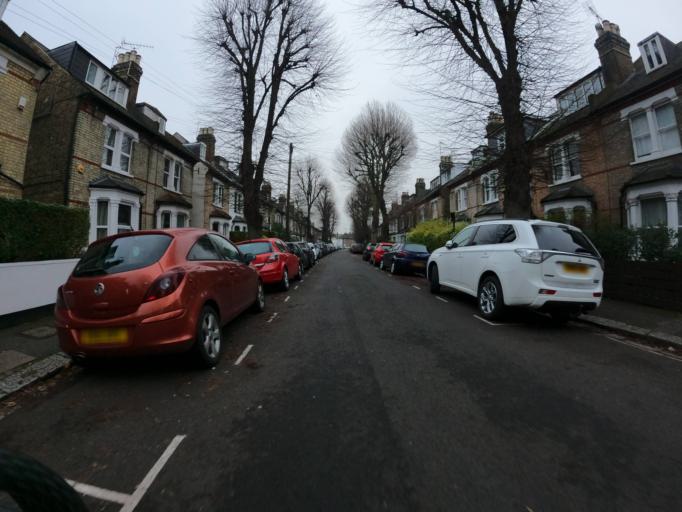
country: GB
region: England
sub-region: Greater London
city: Brentford
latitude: 51.4916
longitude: -0.3099
